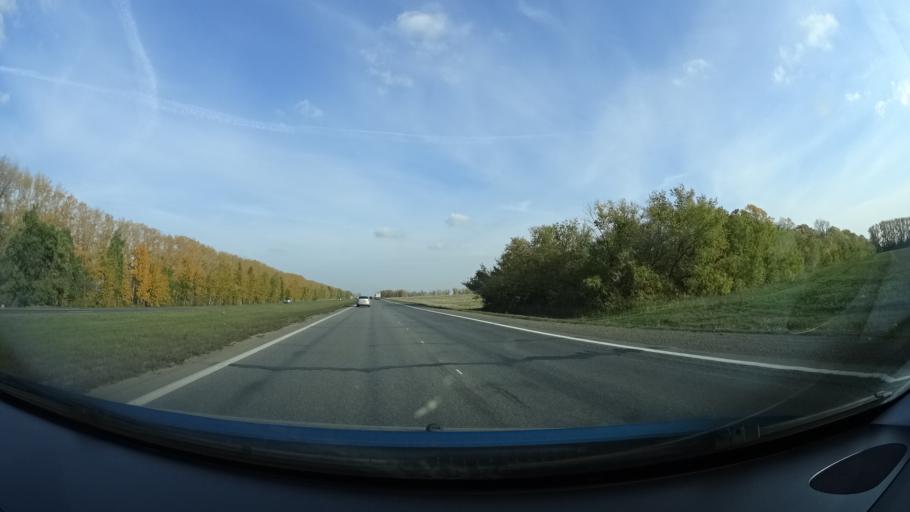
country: RU
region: Bashkortostan
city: Chishmy
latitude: 54.6583
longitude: 55.4661
